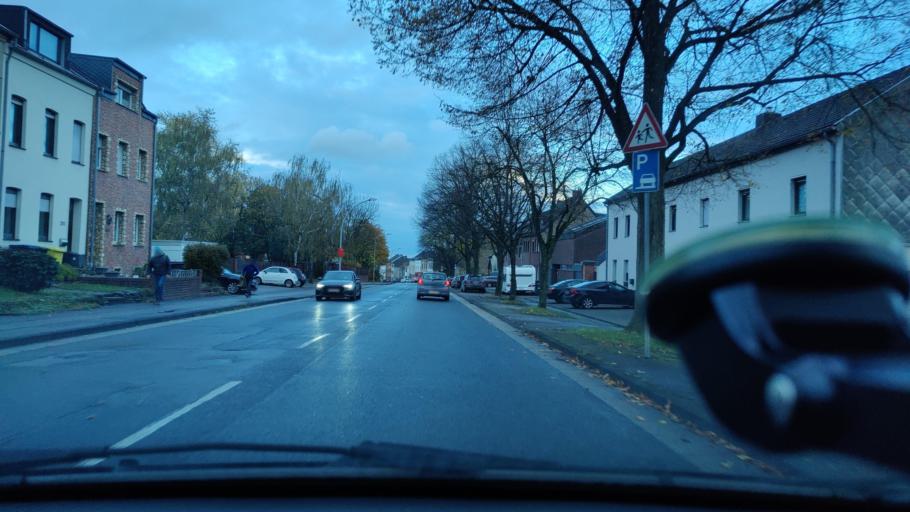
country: DE
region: North Rhine-Westphalia
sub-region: Regierungsbezirk Koln
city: Eschweiler
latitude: 50.8214
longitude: 6.2316
